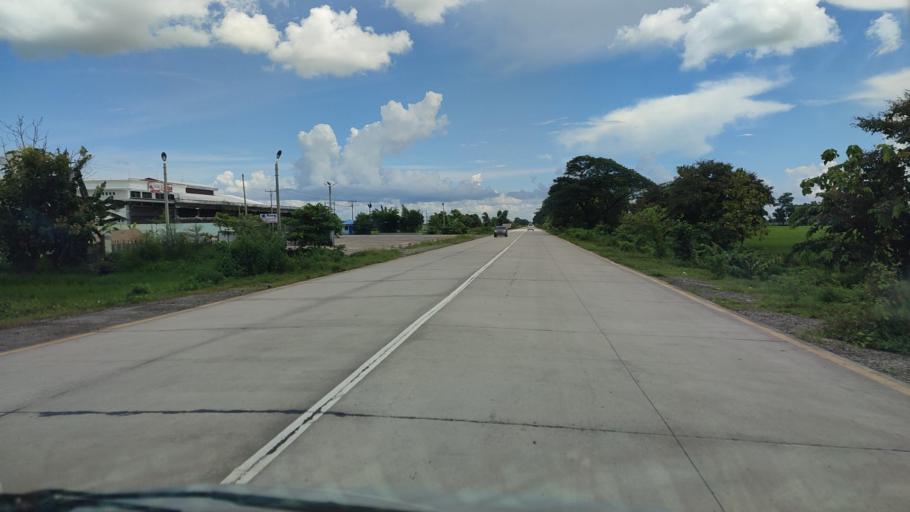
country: MM
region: Bago
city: Nyaunglebin
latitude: 17.9967
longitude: 96.7043
